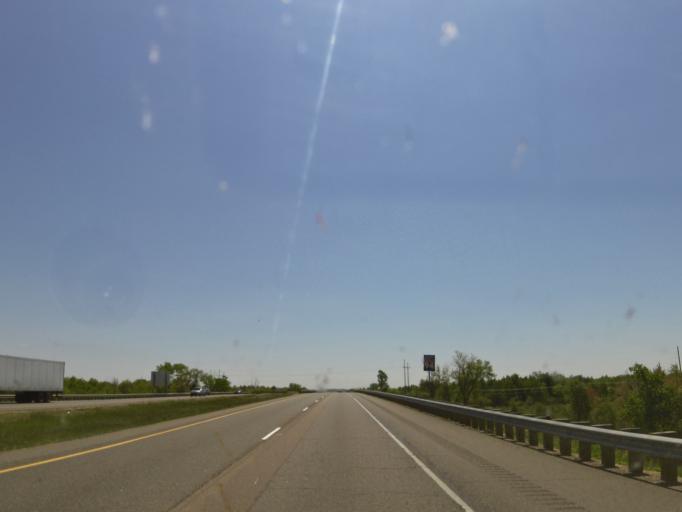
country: US
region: Wisconsin
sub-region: Monroe County
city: Tomah
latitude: 44.0139
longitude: -90.4912
